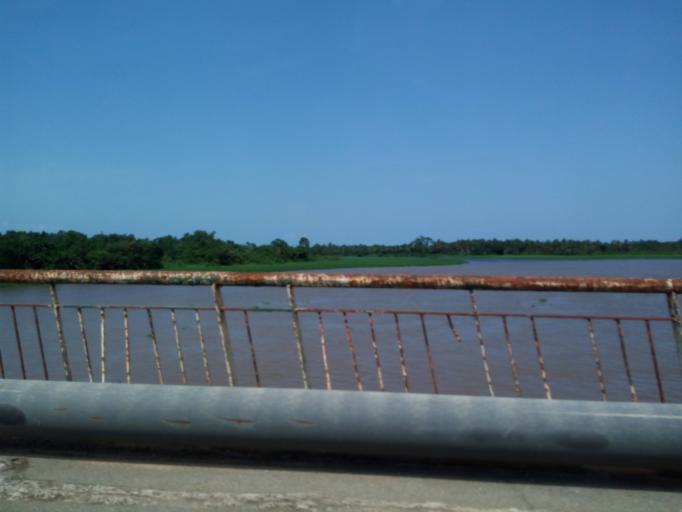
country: CI
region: Sud-Comoe
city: Grand-Bassam
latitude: 5.2170
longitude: -3.7167
